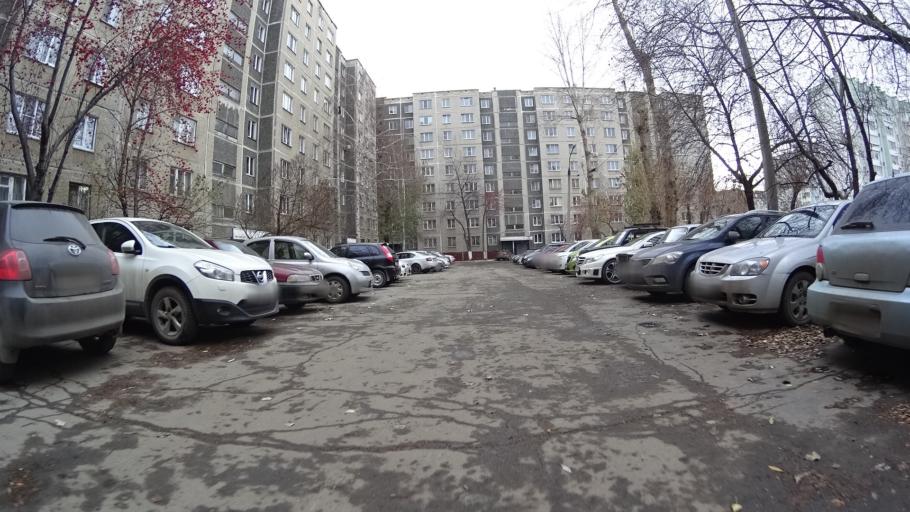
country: RU
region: Chelyabinsk
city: Roshchino
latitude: 55.1868
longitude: 61.2916
